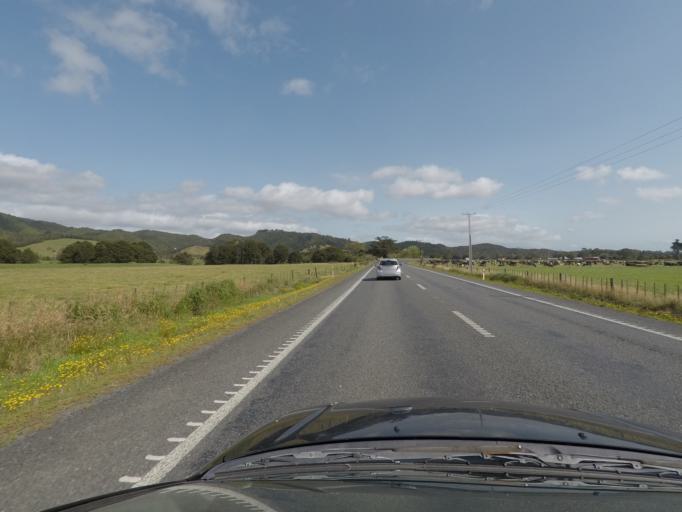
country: NZ
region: Northland
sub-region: Whangarei
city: Ruakaka
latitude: -36.0050
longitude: 174.4152
